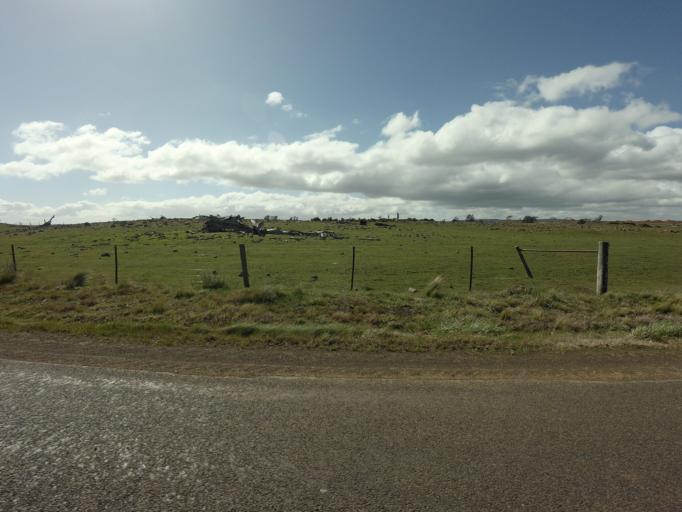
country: AU
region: Tasmania
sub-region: Northern Midlands
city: Evandale
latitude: -41.8988
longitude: 147.4367
